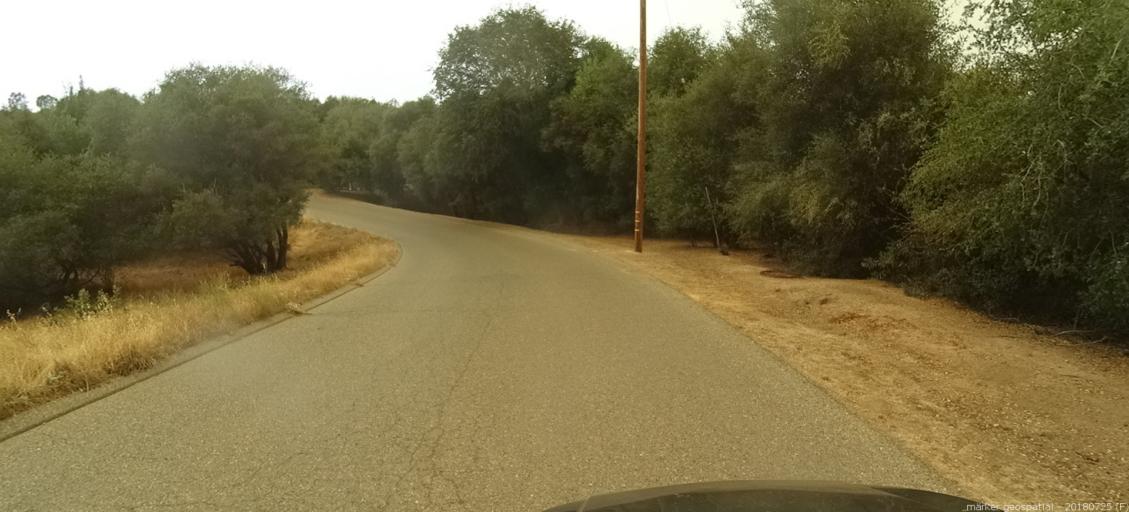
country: US
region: California
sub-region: Madera County
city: Coarsegold
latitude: 37.2025
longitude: -119.6830
